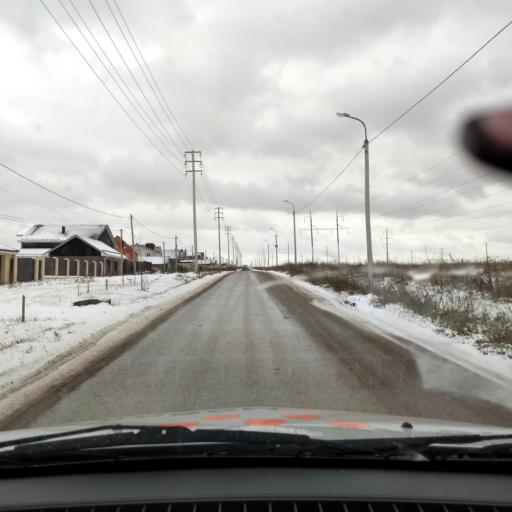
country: RU
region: Bashkortostan
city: Kabakovo
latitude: 54.6173
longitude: 56.0902
